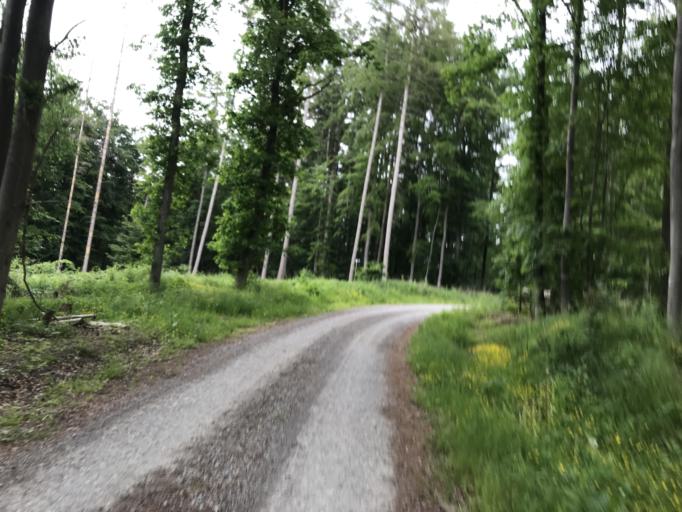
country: DE
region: Hesse
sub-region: Regierungsbezirk Kassel
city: Martinhagen
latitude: 51.2942
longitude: 9.2666
